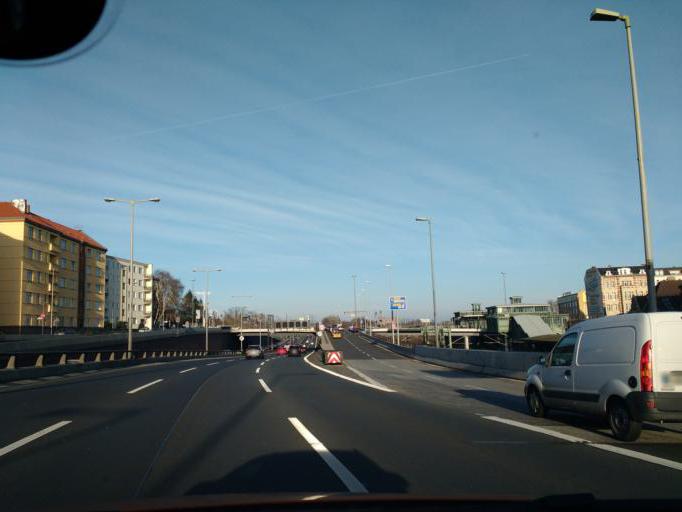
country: DE
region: Berlin
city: Charlottenburg Bezirk
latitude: 52.5169
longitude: 13.2842
